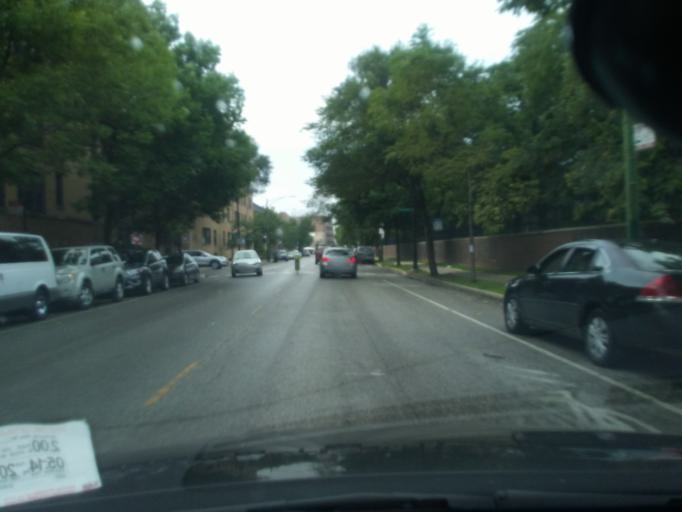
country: US
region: Illinois
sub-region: Cook County
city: Lincolnwood
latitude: 41.9595
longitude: -87.6651
